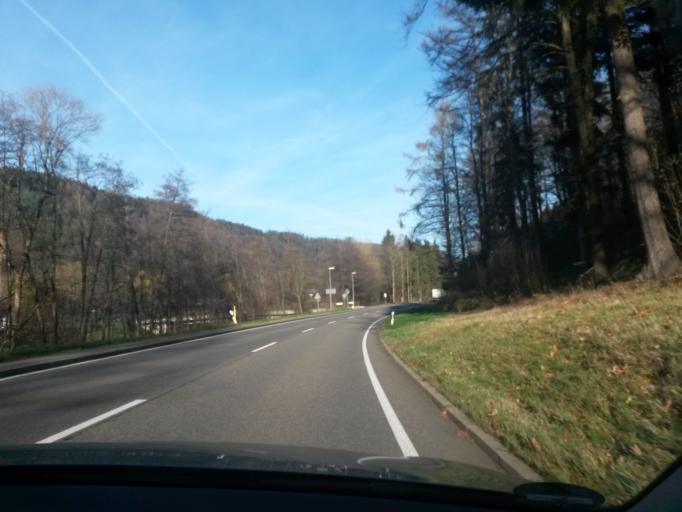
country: DE
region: Baden-Wuerttemberg
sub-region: Karlsruhe Region
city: Neuenburg
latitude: 48.8270
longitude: 8.5790
